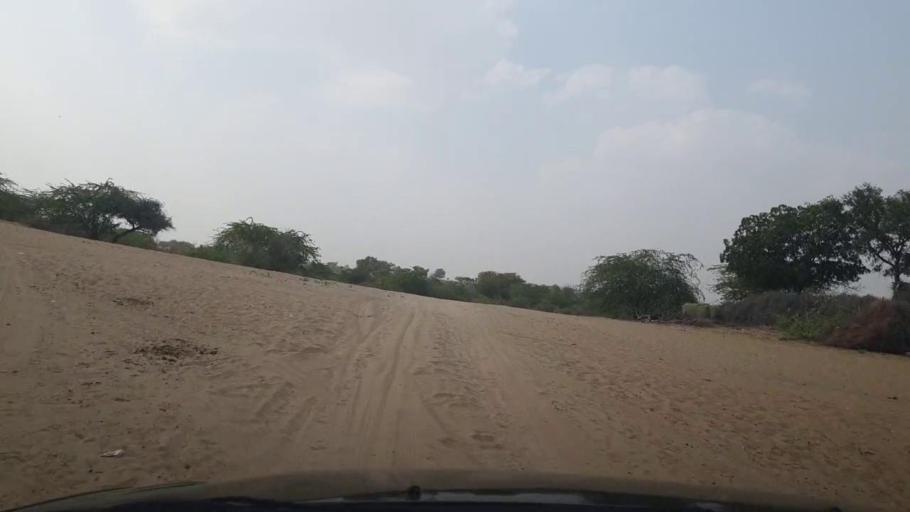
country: PK
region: Sindh
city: Islamkot
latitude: 24.9571
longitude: 70.6326
